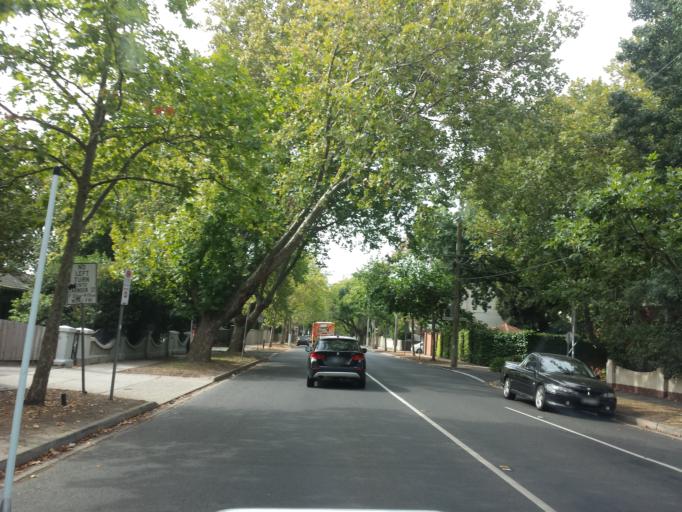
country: AU
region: Victoria
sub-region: Port Phillip
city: St Kilda East
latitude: -37.8580
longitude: 145.0109
